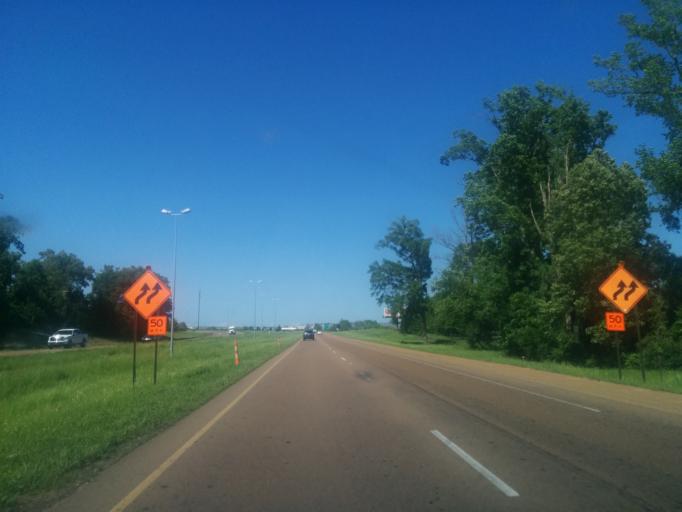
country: US
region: Mississippi
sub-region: Madison County
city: Madison
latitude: 32.5219
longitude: -90.0982
